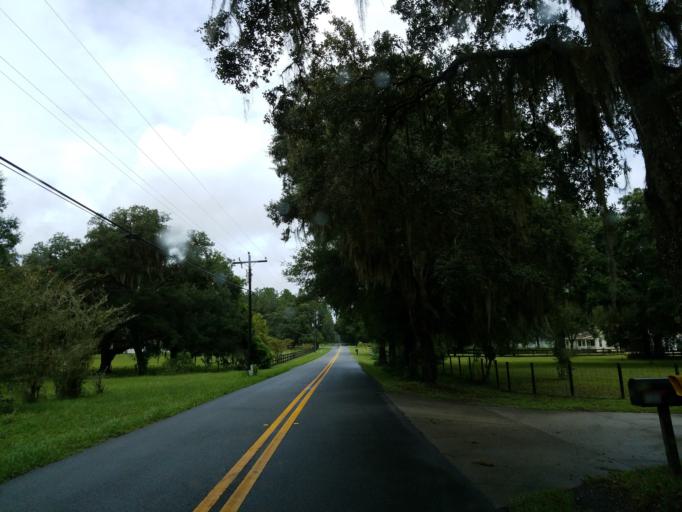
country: US
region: Florida
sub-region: Citrus County
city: Inverness Highlands South
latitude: 28.7976
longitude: -82.2951
